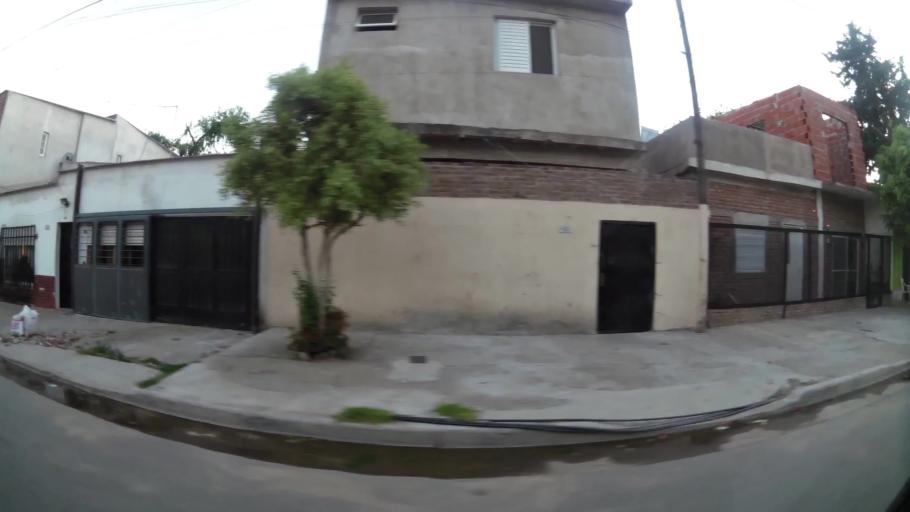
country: AR
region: Santa Fe
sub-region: Departamento de Rosario
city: Rosario
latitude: -32.9586
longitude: -60.6874
